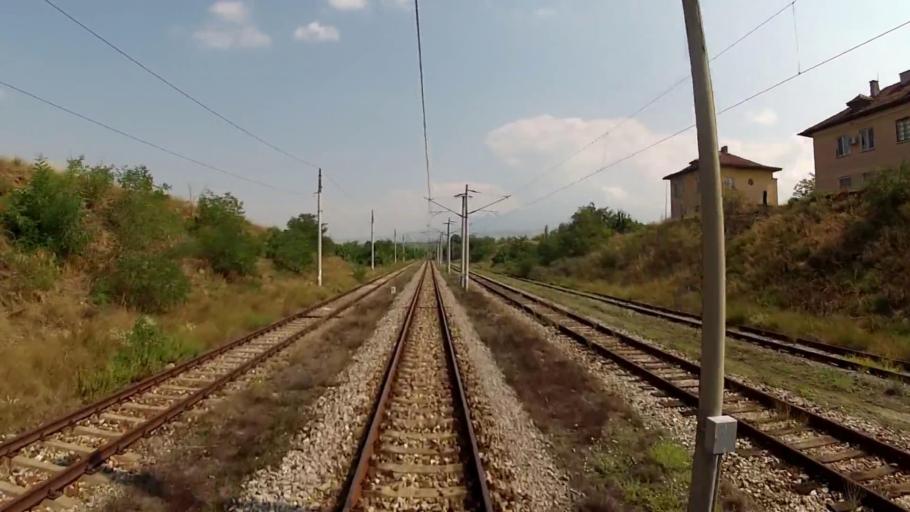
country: BG
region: Blagoevgrad
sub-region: Obshtina Sandanski
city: Sandanski
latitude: 41.5546
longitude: 23.2505
